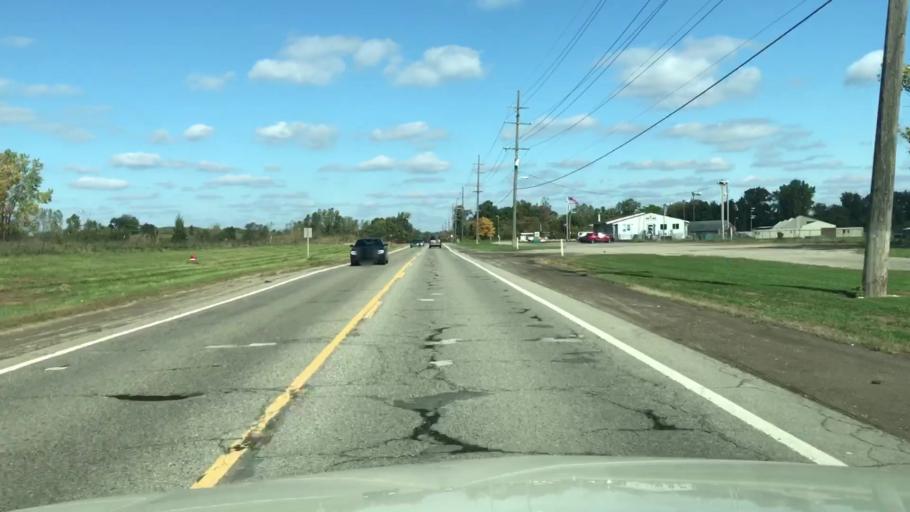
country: US
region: Michigan
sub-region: Oakland County
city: Rochester
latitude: 42.6555
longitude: -83.0929
